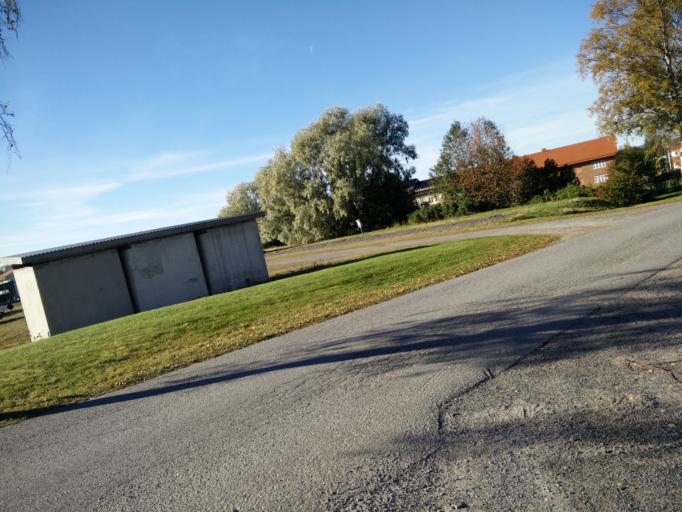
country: SE
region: Vaesternorrland
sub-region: Haernoesands Kommun
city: Haernoesand
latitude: 62.6404
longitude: 17.9642
